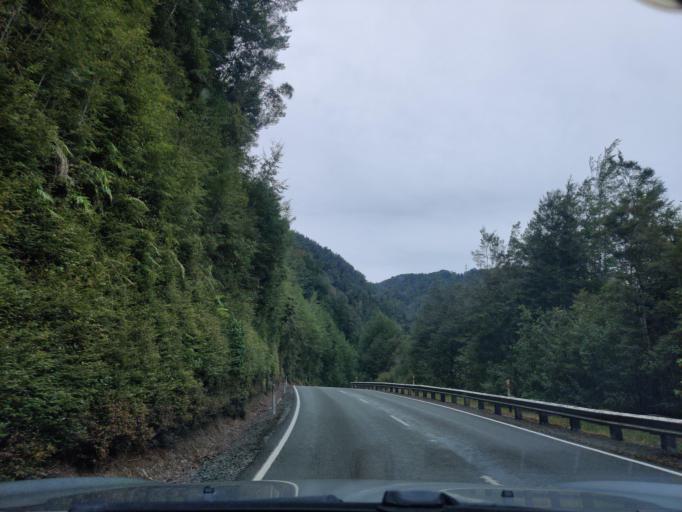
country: NZ
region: West Coast
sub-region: Buller District
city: Westport
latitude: -41.7728
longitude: 172.1471
